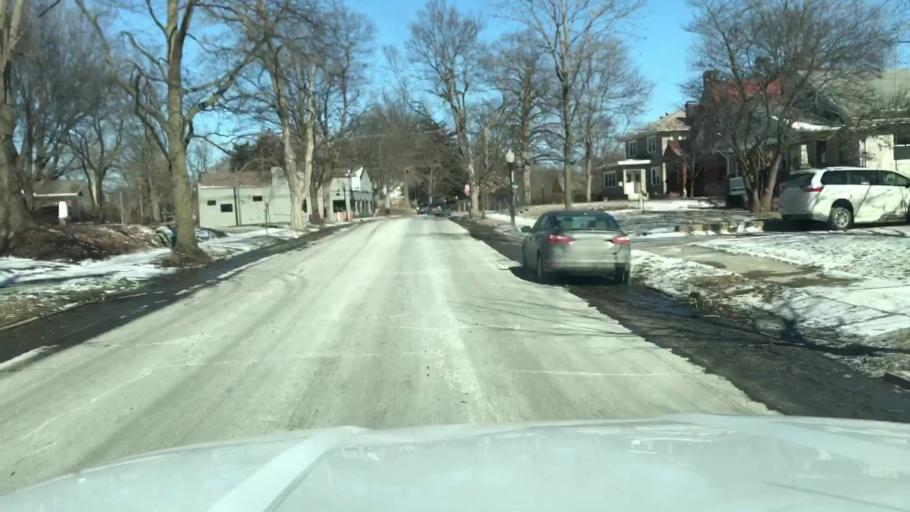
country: US
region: Missouri
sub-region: Buchanan County
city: Saint Joseph
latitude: 39.7912
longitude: -94.8211
